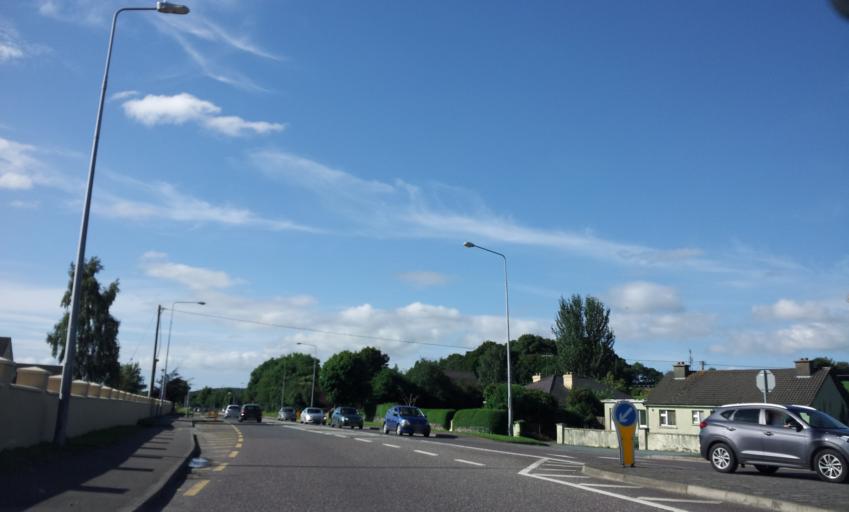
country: IE
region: Munster
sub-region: Ciarrai
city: Cill Airne
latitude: 52.0508
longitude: -9.4577
